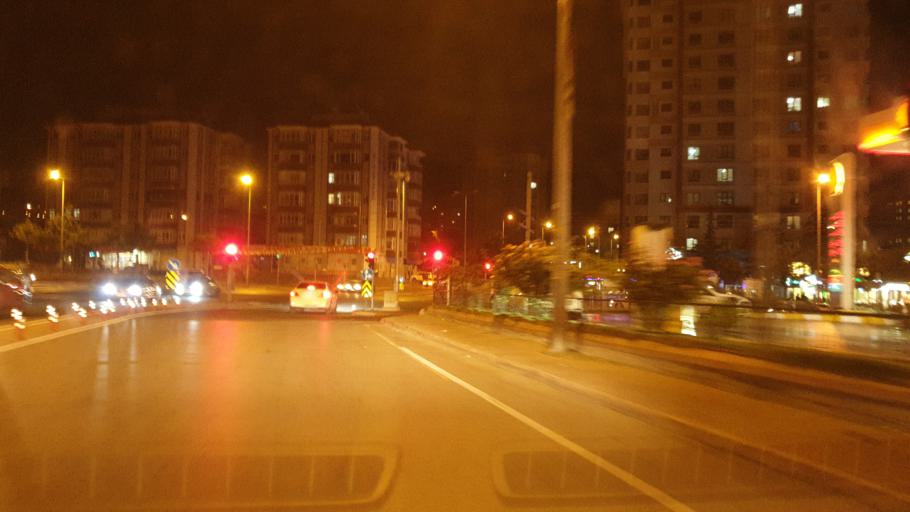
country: TR
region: Kayseri
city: Talas
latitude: 38.6944
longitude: 35.5459
